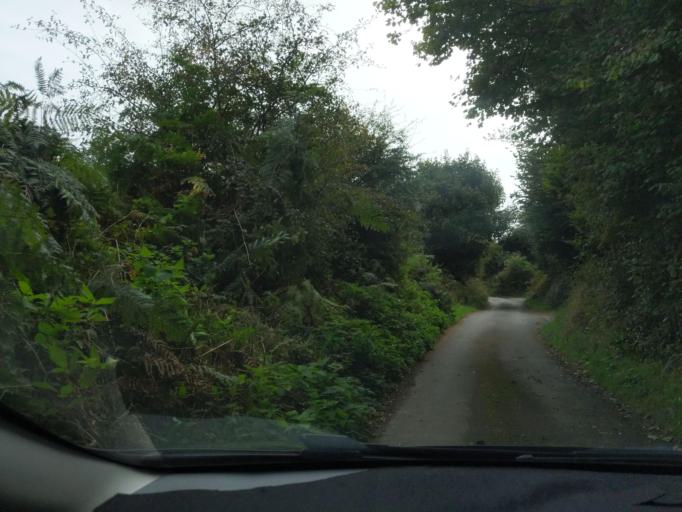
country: GB
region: England
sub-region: Cornwall
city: Lostwithiel
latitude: 50.3928
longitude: -4.7048
